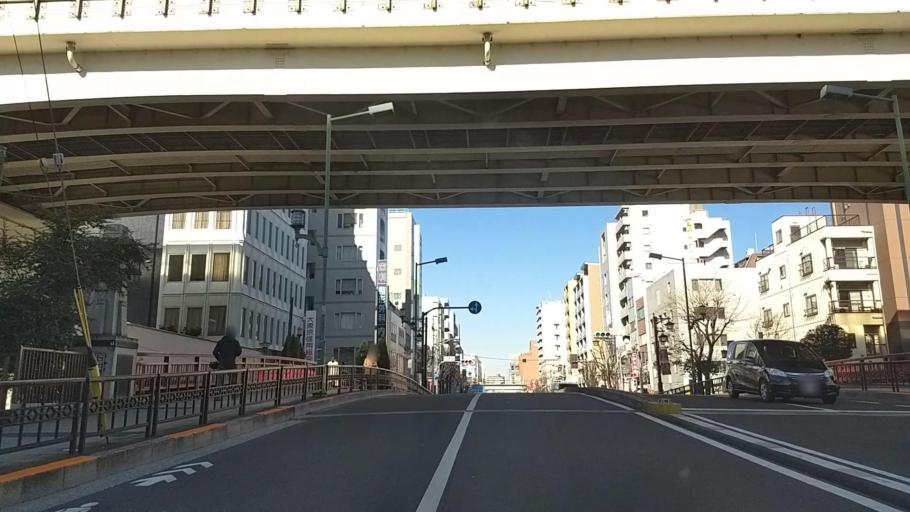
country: JP
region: Tokyo
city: Urayasu
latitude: 35.6935
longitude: 139.8260
